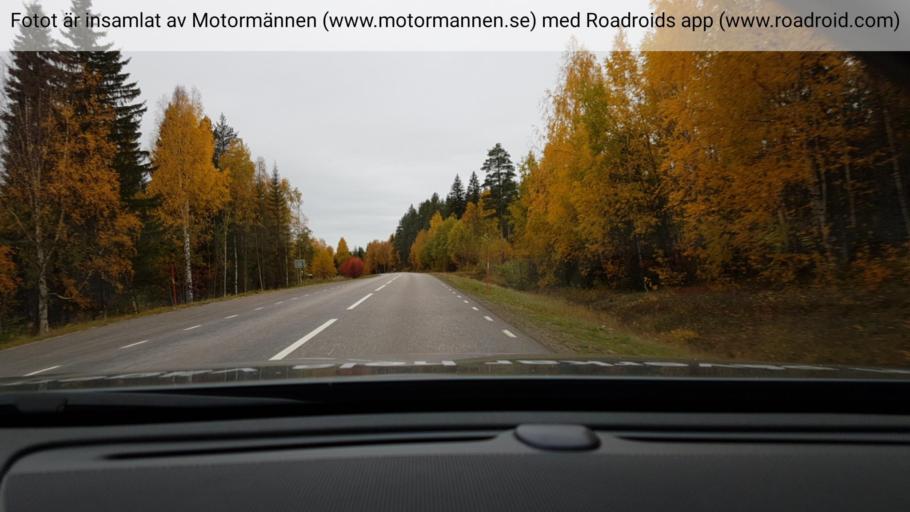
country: SE
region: Norrbotten
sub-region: Overkalix Kommun
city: OEverkalix
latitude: 66.4924
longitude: 22.7761
